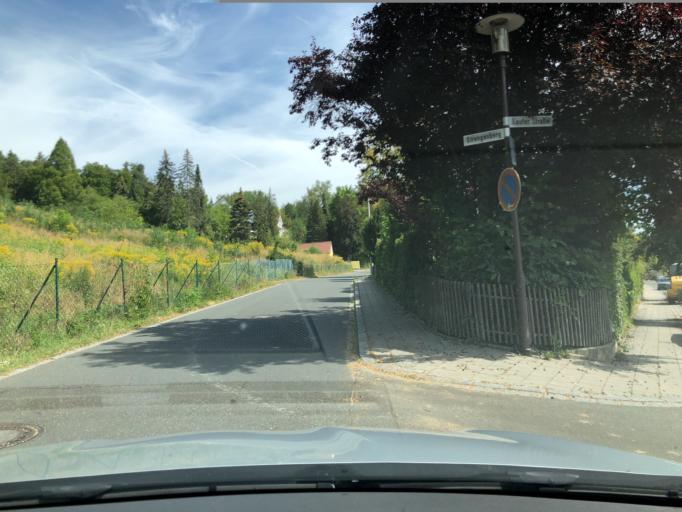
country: DE
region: Bavaria
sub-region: Regierungsbezirk Mittelfranken
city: Ruckersdorf
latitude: 49.5026
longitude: 11.2553
